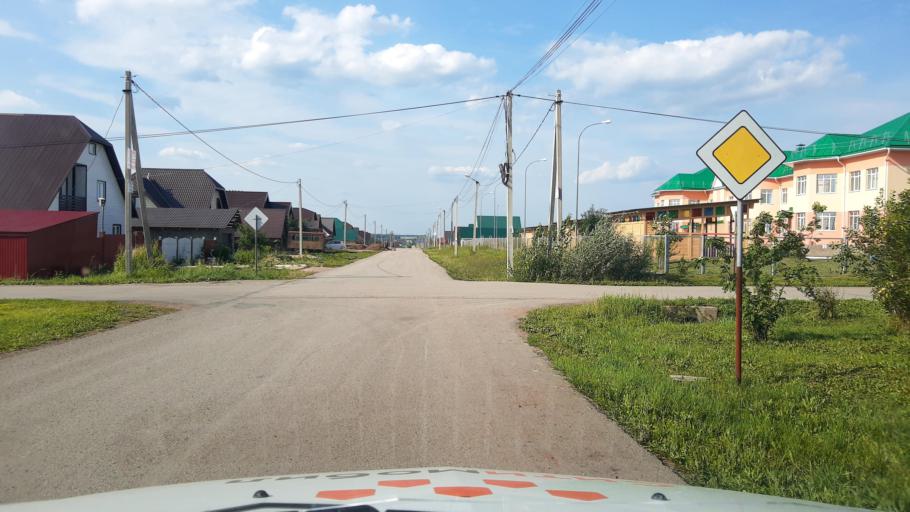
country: RU
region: Bashkortostan
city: Kabakovo
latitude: 54.6522
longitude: 56.2126
